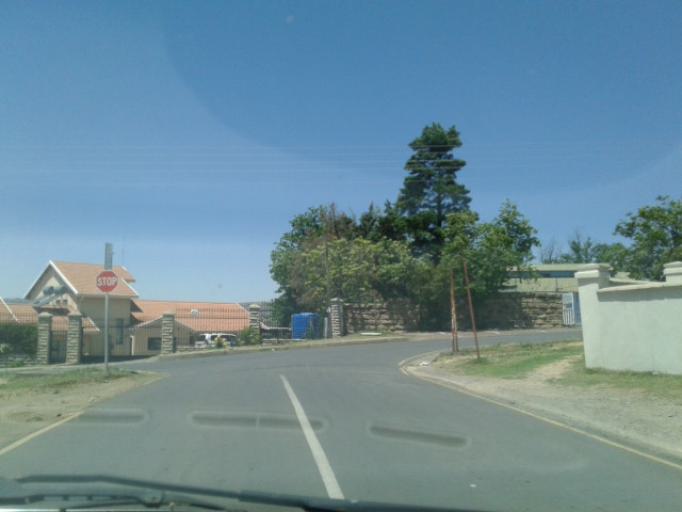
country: LS
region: Maseru
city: Maseru
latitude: -29.3007
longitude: 27.4796
